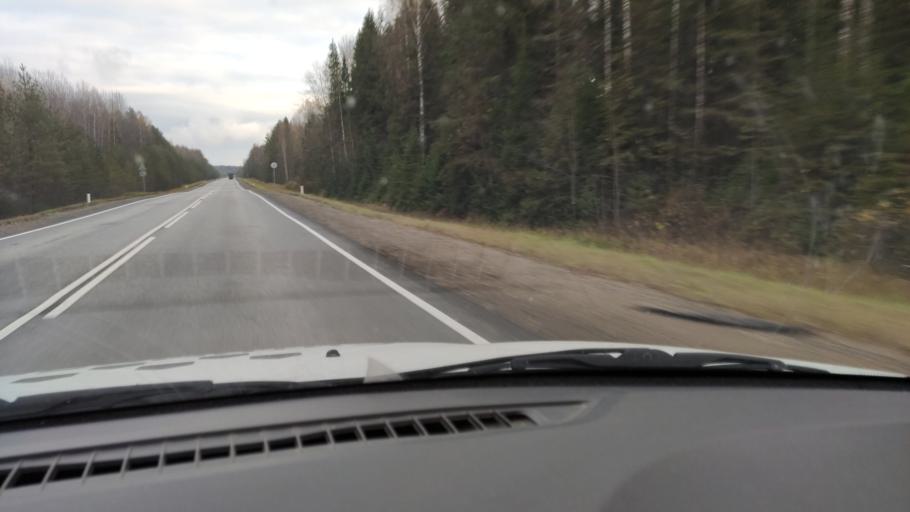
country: RU
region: Kirov
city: Chernaya Kholunitsa
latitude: 58.8295
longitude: 51.7659
